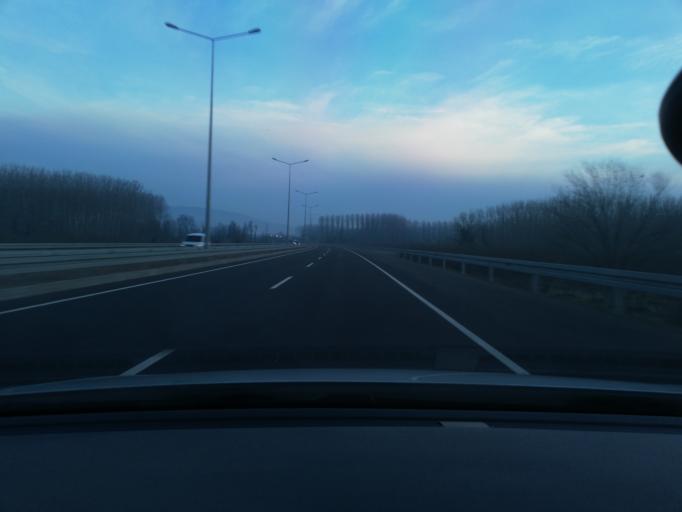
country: TR
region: Duzce
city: Duzce
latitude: 40.8101
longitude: 31.1691
